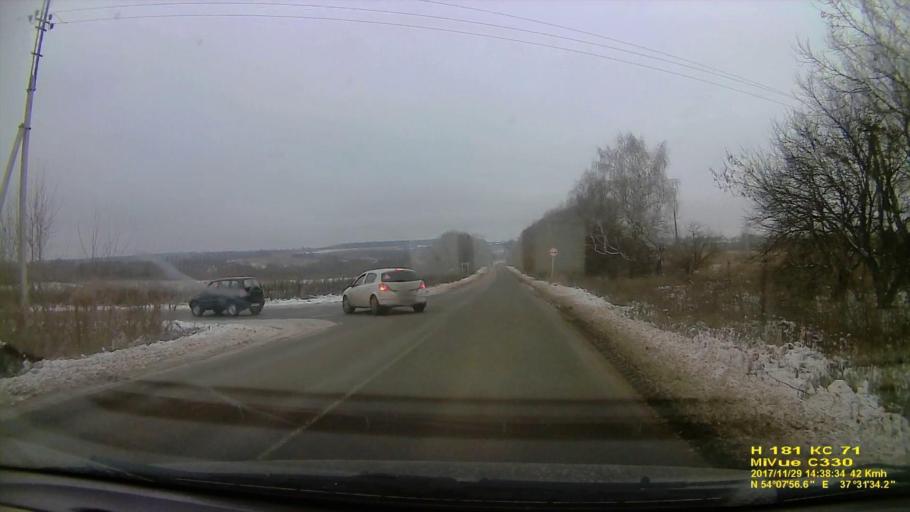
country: RU
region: Tula
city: Kosaya Gora
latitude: 54.1351
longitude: 37.5287
